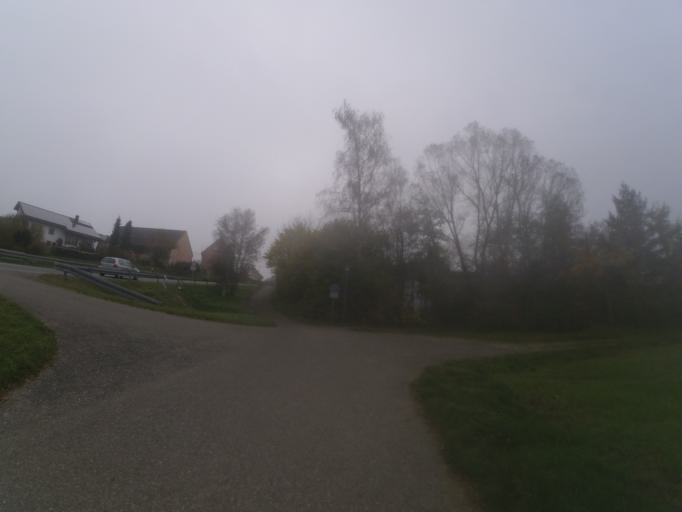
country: DE
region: Baden-Wuerttemberg
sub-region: Tuebingen Region
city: Staig
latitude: 48.3421
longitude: 9.9980
